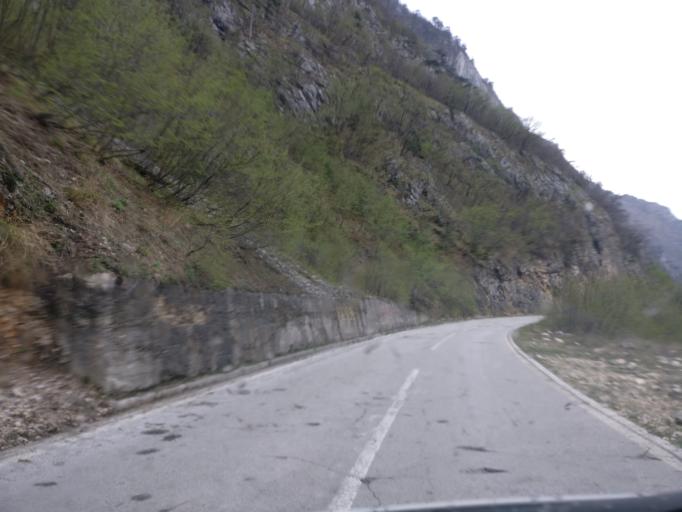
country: ME
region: Opstina Pluzine
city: Pluzine
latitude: 43.2103
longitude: 18.8593
